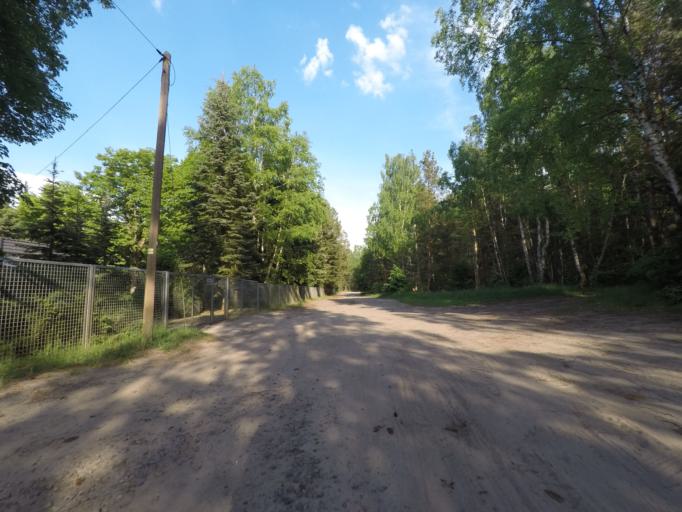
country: DE
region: Brandenburg
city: Melchow
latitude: 52.8318
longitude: 13.7260
